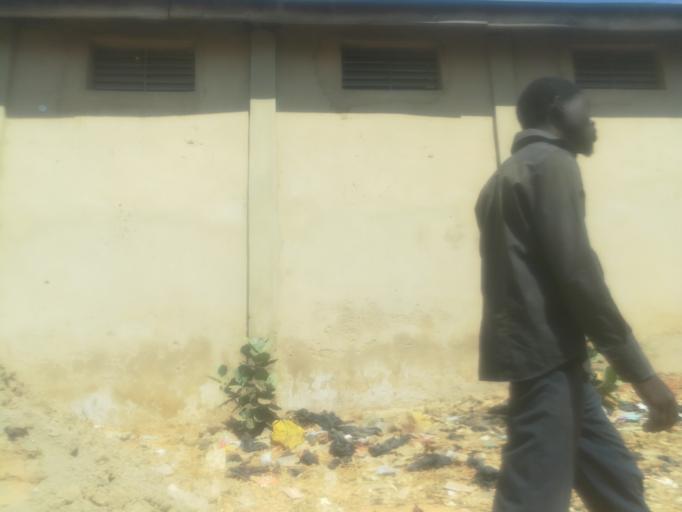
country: NG
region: Kano
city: Kano
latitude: 12.0019
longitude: 8.5363
